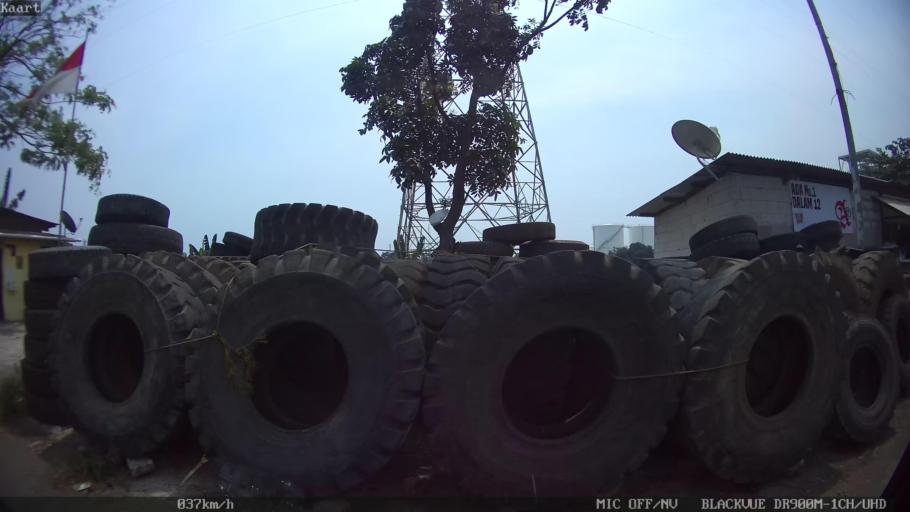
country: ID
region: Banten
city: Curug
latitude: -5.9647
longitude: 106.0058
